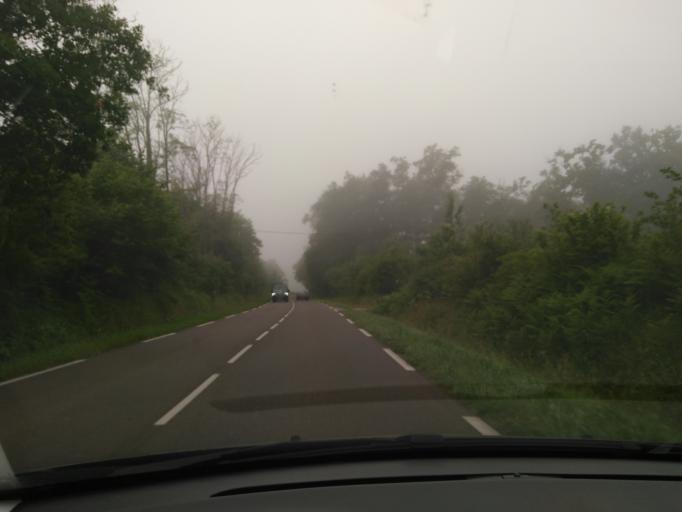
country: FR
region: Aquitaine
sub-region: Departement des Landes
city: Villeneuve-de-Marsan
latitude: 43.8893
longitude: -0.4029
